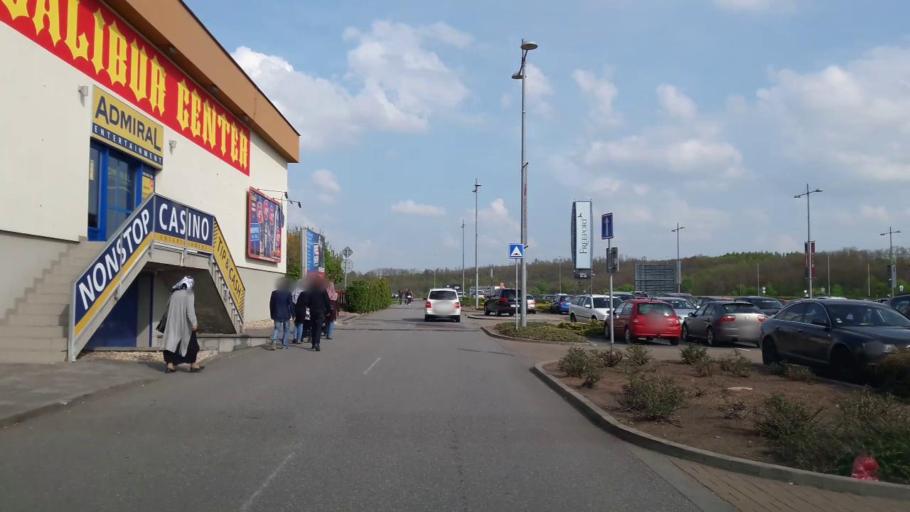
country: CZ
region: South Moravian
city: Vrbovec
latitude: 48.7639
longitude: 16.0634
